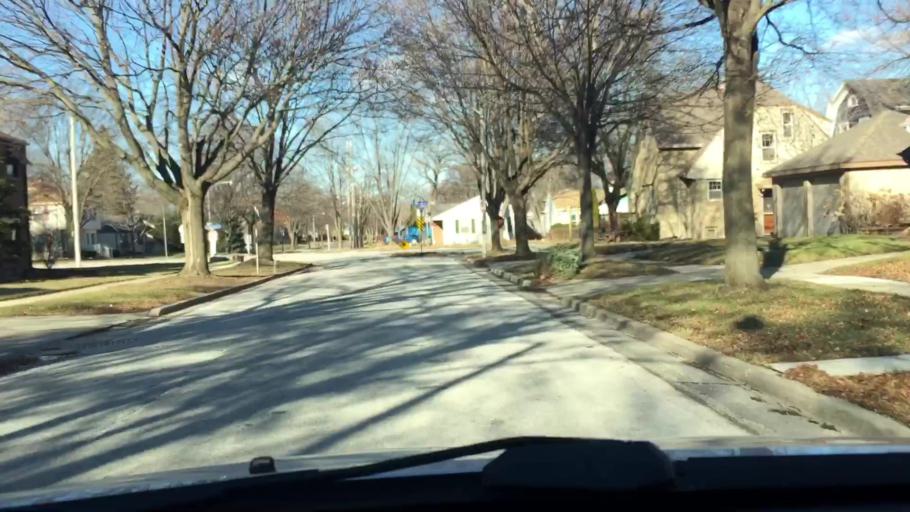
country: US
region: Wisconsin
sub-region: Milwaukee County
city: Wauwatosa
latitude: 43.0353
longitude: -87.9998
